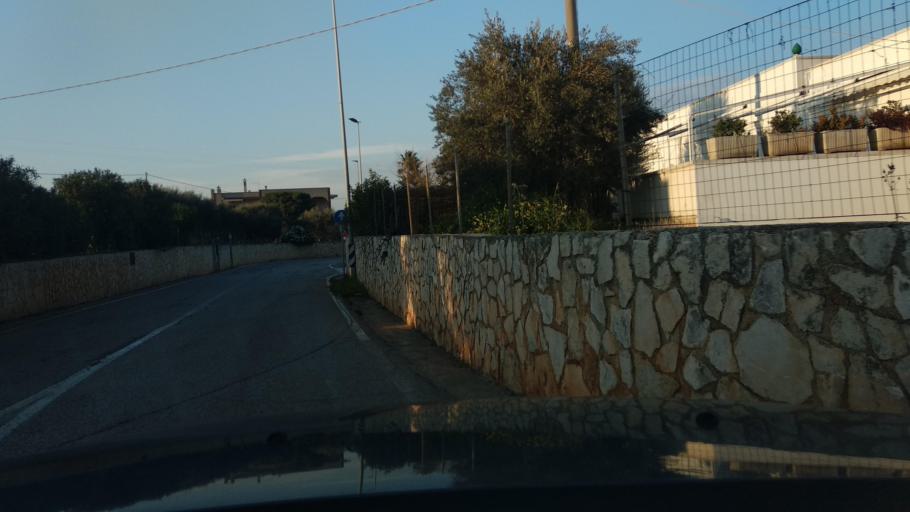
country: IT
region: Apulia
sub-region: Provincia di Brindisi
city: Fasano
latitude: 40.8807
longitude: 17.3376
